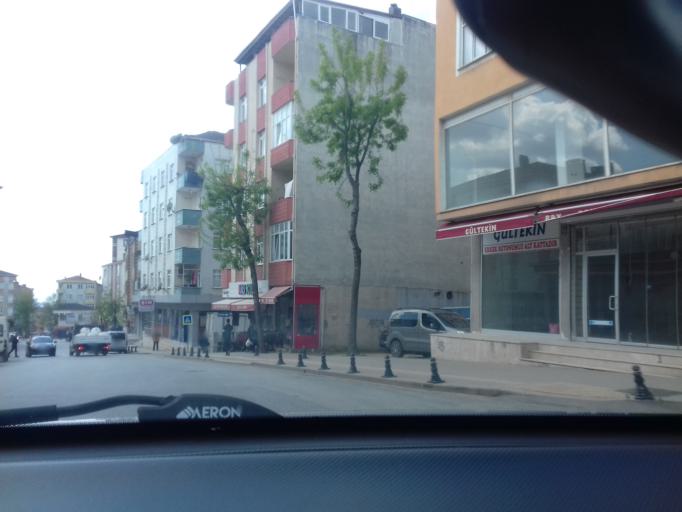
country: TR
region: Istanbul
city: Pendik
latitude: 40.8753
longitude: 29.2847
